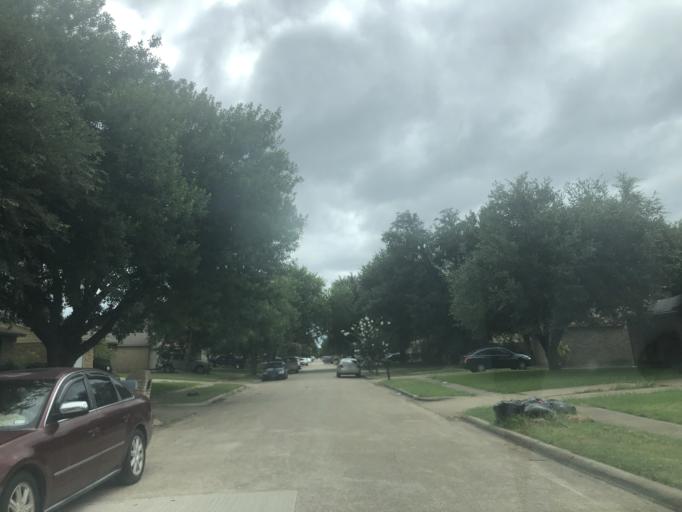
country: US
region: Texas
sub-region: Dallas County
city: Duncanville
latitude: 32.6443
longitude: -96.9514
